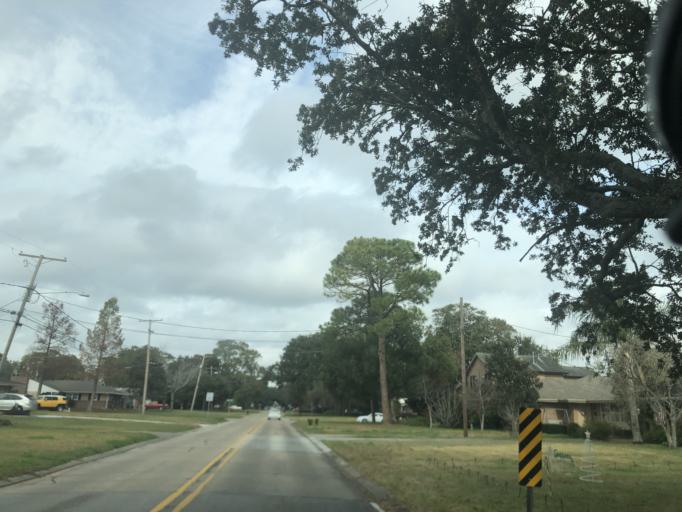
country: US
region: Louisiana
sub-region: Jefferson Parish
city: Metairie Terrace
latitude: 29.9845
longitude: -90.1602
